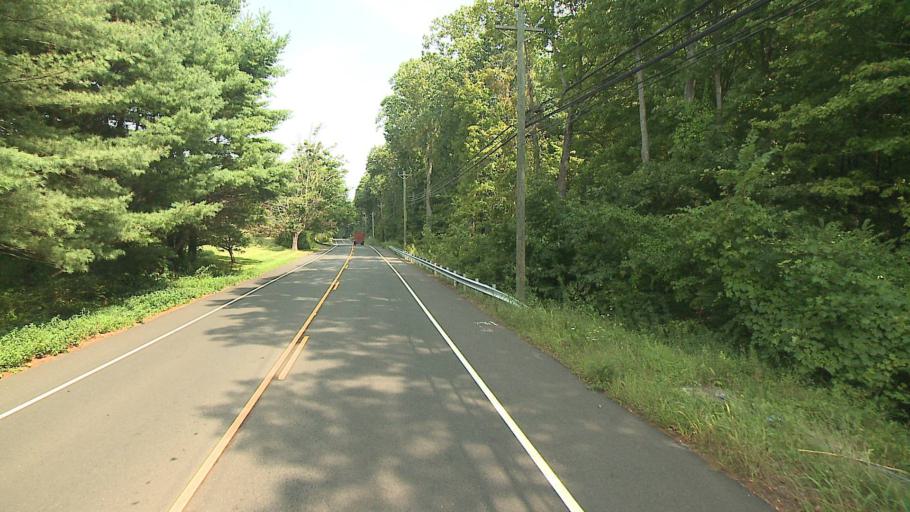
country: US
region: Connecticut
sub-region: Fairfield County
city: Bethel
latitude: 41.3157
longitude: -73.3854
